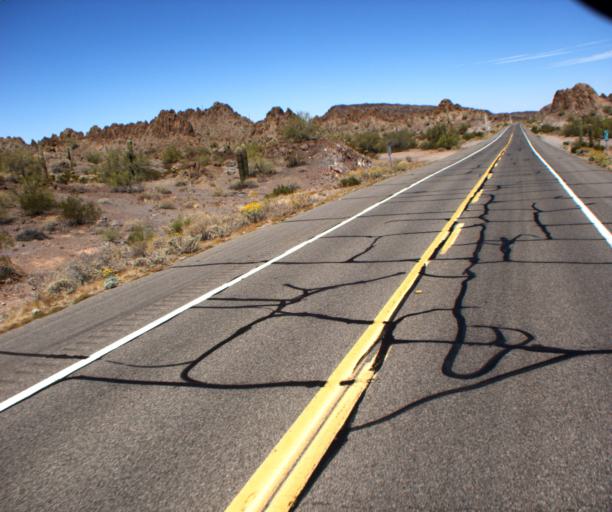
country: US
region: Arizona
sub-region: Pima County
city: Ajo
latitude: 32.5417
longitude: -112.8800
